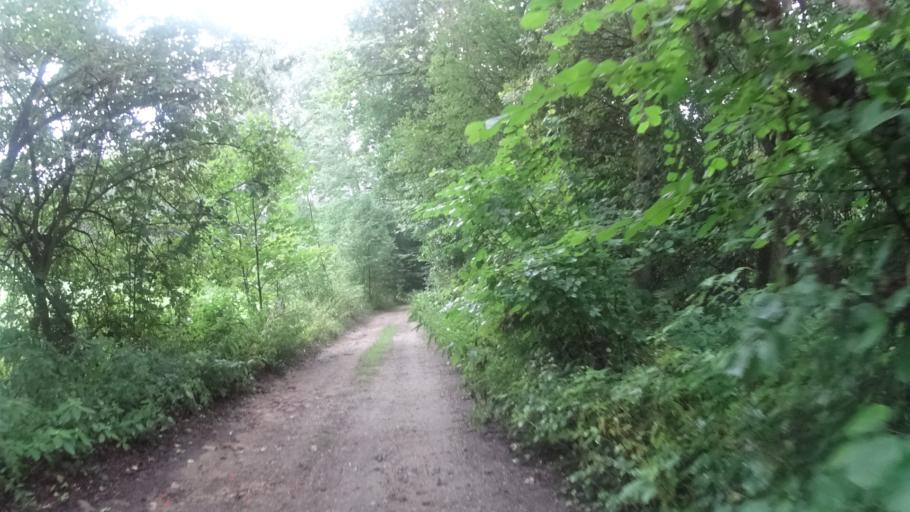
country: DE
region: Schleswig-Holstein
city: Siebeneichen
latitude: 53.4986
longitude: 10.6207
